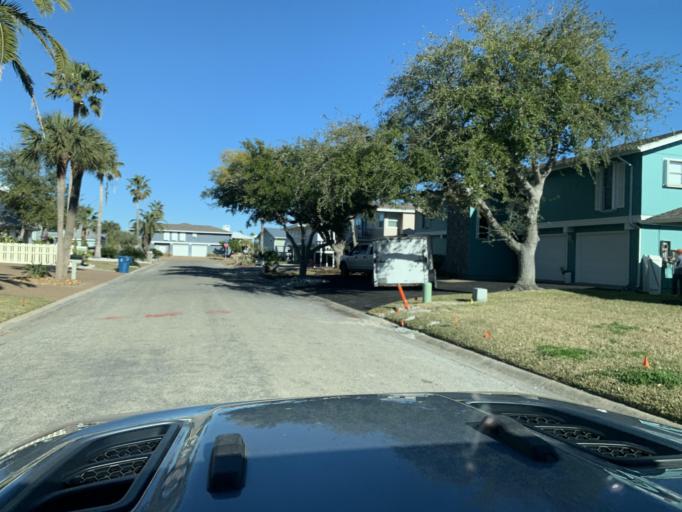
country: US
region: Texas
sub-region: Aransas County
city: Fulton
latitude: 28.0362
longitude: -97.0304
